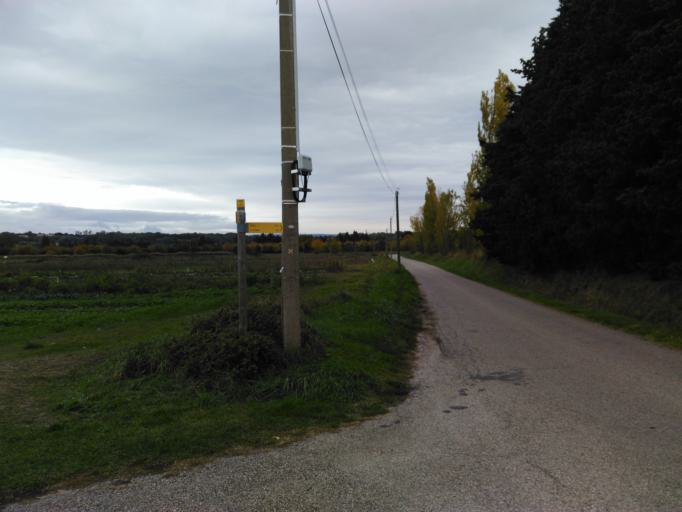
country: FR
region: Provence-Alpes-Cote d'Azur
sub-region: Departement du Vaucluse
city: Grillon
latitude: 44.3865
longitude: 4.9163
